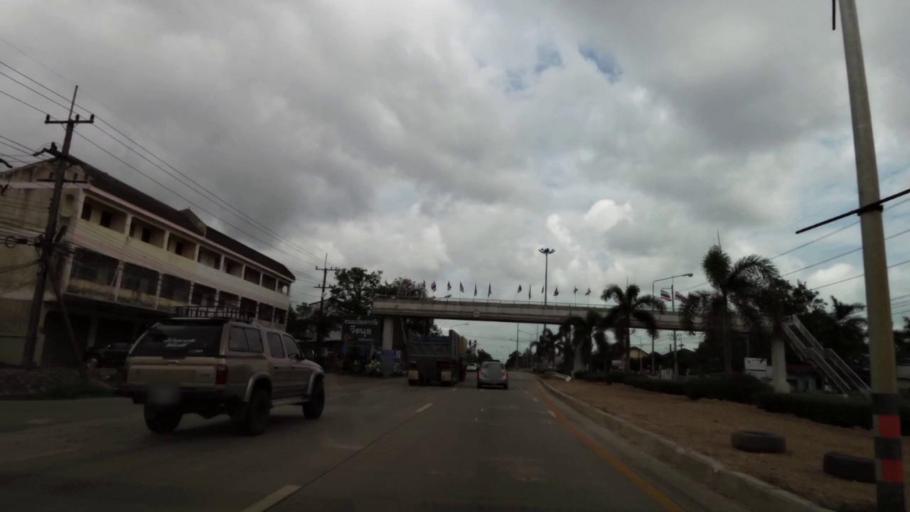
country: TH
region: Chanthaburi
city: Na Yai Am
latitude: 12.7814
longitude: 101.8092
